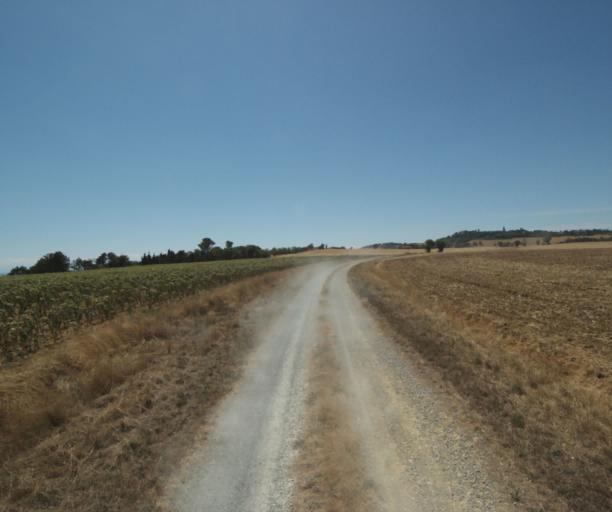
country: FR
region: Midi-Pyrenees
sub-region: Departement de la Haute-Garonne
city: Saint-Felix-Lauragais
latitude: 43.4566
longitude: 1.9093
